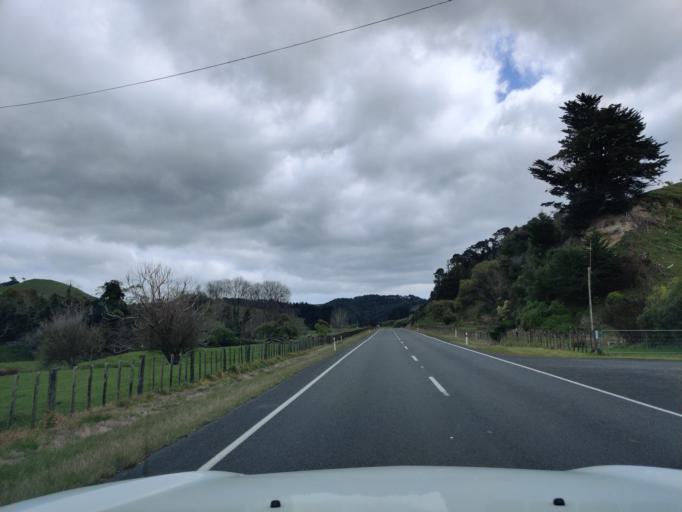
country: NZ
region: Manawatu-Wanganui
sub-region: Wanganui District
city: Wanganui
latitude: -39.8484
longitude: 175.1393
